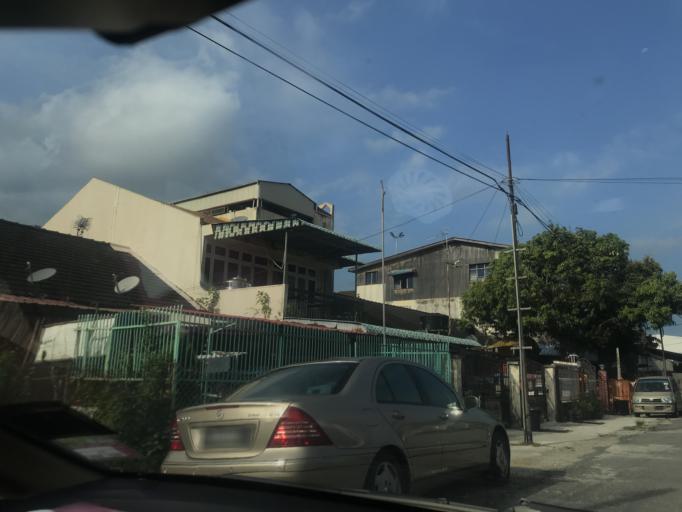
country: MY
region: Kelantan
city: Kota Bharu
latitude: 6.1159
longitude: 102.2398
